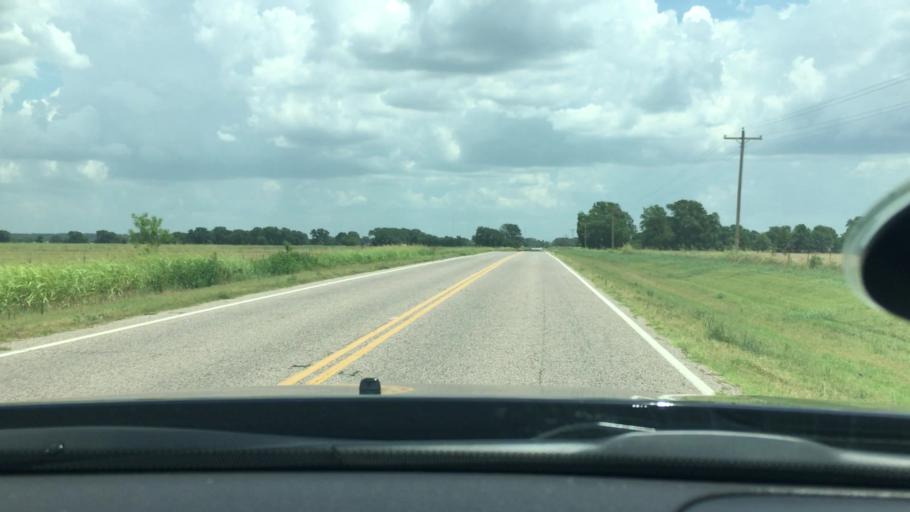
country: US
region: Texas
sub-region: Grayson County
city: Sherwood Shores
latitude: 33.9840
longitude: -96.9320
